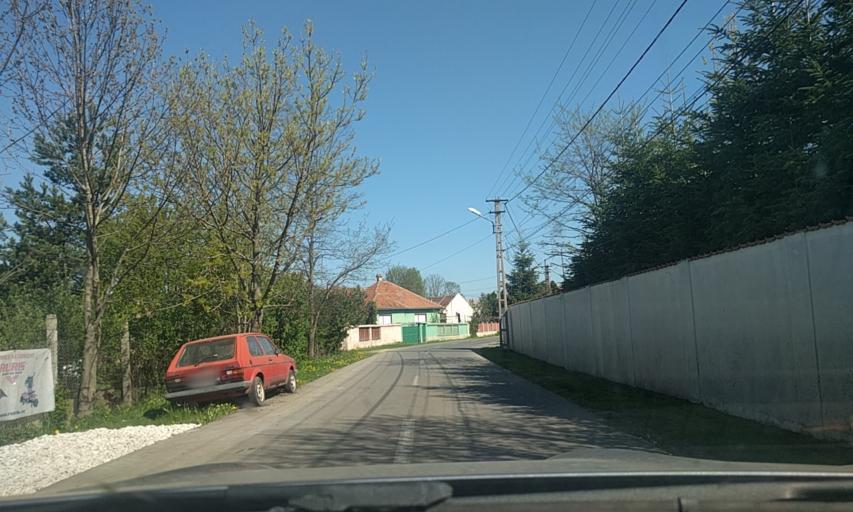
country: RO
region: Brasov
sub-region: Comuna Bod
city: Colonia Bod
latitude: 45.7089
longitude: 25.5753
